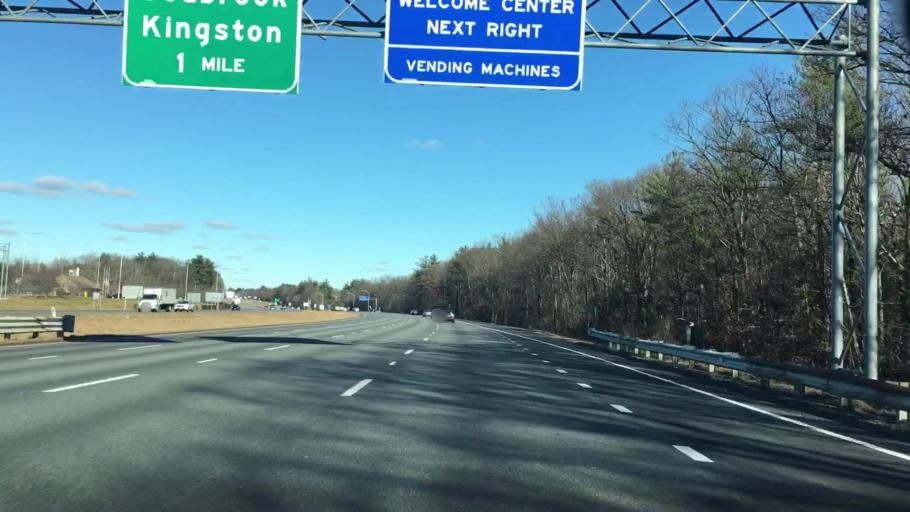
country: US
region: New Hampshire
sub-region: Rockingham County
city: Seabrook
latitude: 42.8770
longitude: -70.8846
